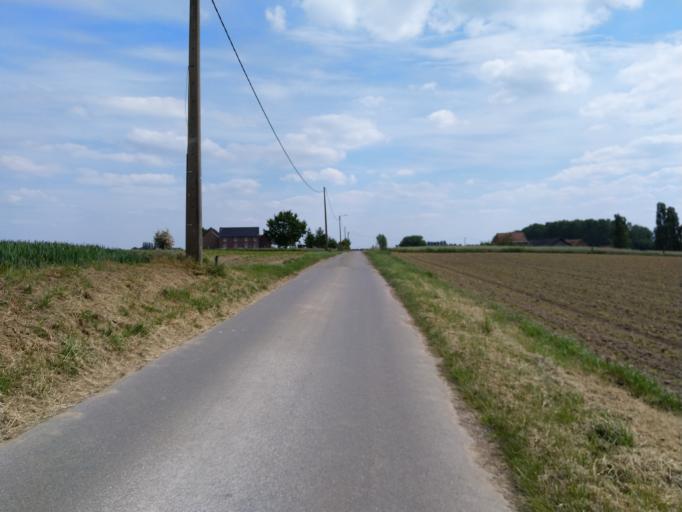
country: BE
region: Wallonia
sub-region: Province du Hainaut
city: Silly
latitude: 50.5884
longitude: 3.9688
